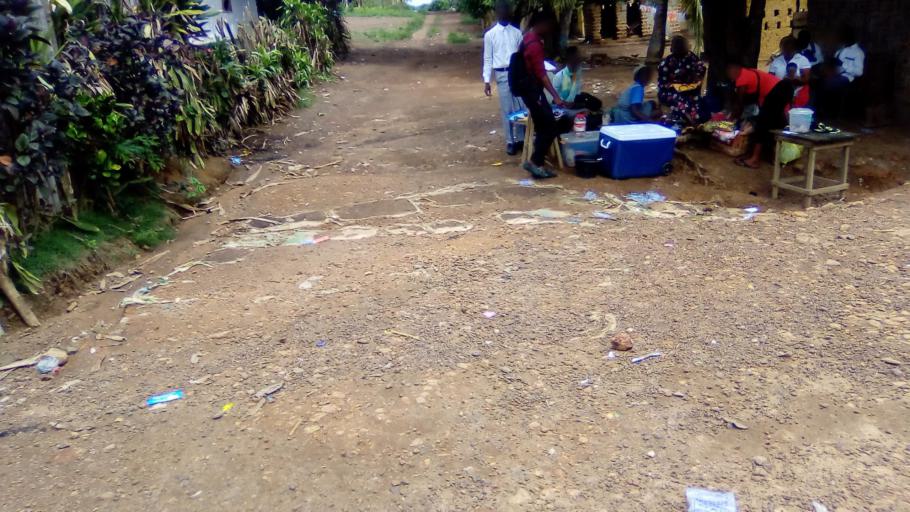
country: SL
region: Southern Province
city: Bo
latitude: 7.9337
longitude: -11.7214
